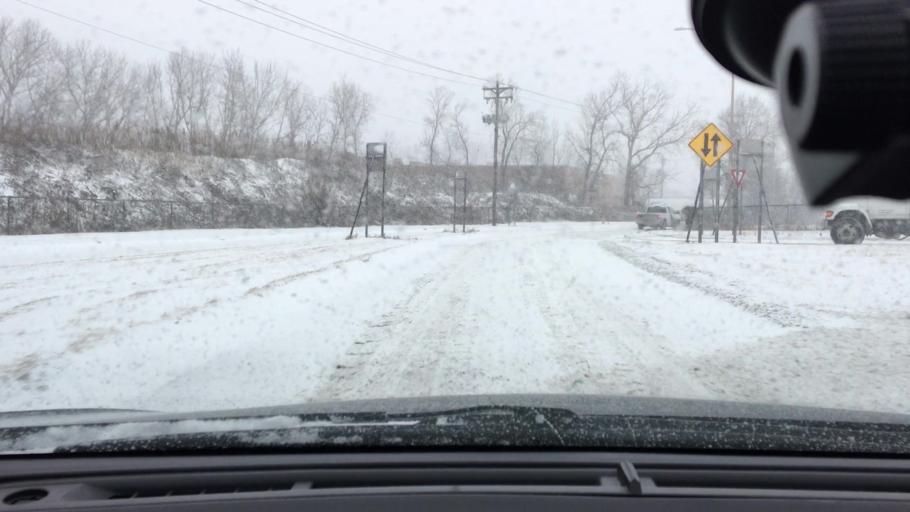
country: US
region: Minnesota
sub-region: Hennepin County
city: New Hope
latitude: 44.9901
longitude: -93.4001
